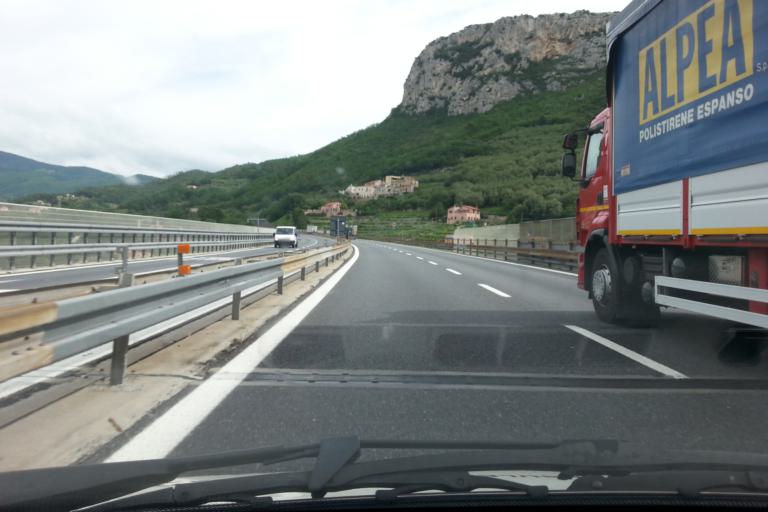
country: IT
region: Liguria
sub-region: Provincia di Savona
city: Calice Ligure
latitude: 44.1879
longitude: 8.3057
